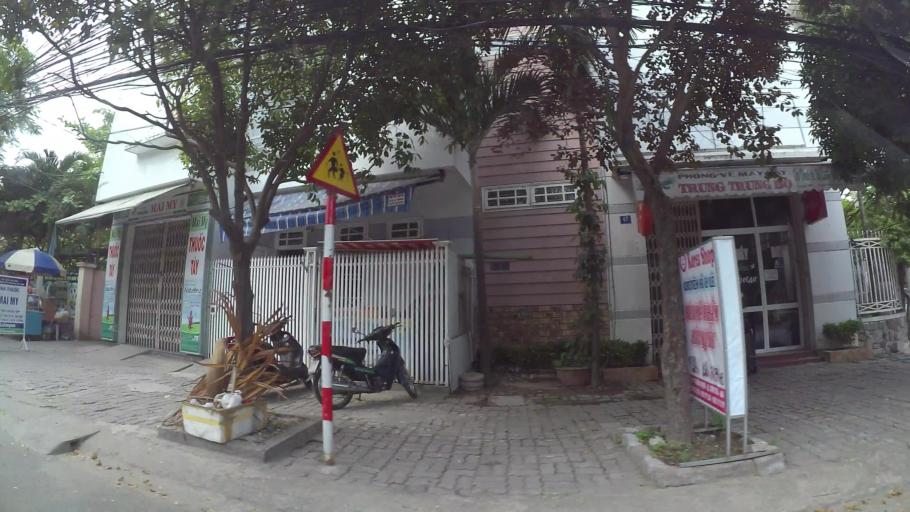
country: VN
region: Da Nang
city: Son Tra
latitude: 16.0895
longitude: 108.2457
